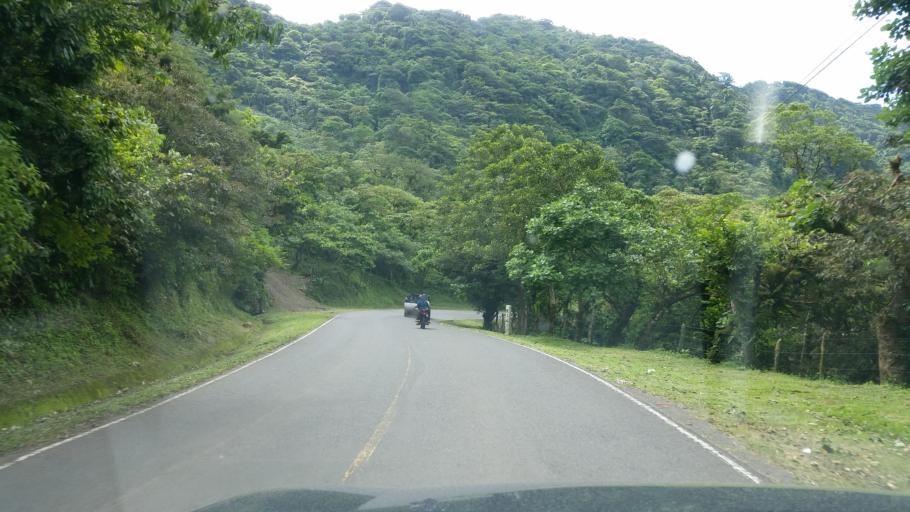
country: NI
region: Matagalpa
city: San Ramon
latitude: 12.9619
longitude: -85.8546
